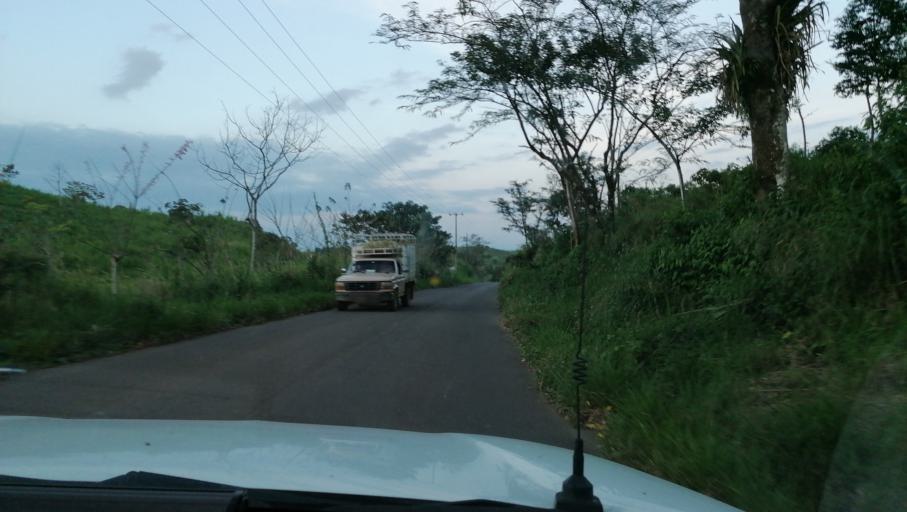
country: MX
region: Chiapas
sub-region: Ostuacan
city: Nuevo Juan del Grijalva
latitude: 17.4369
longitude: -93.3516
